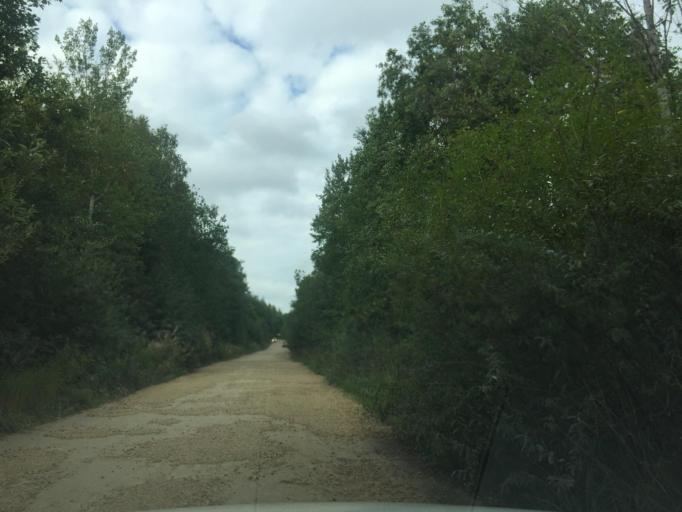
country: RU
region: Leningrad
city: Siverskiy
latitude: 59.2986
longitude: 30.0291
